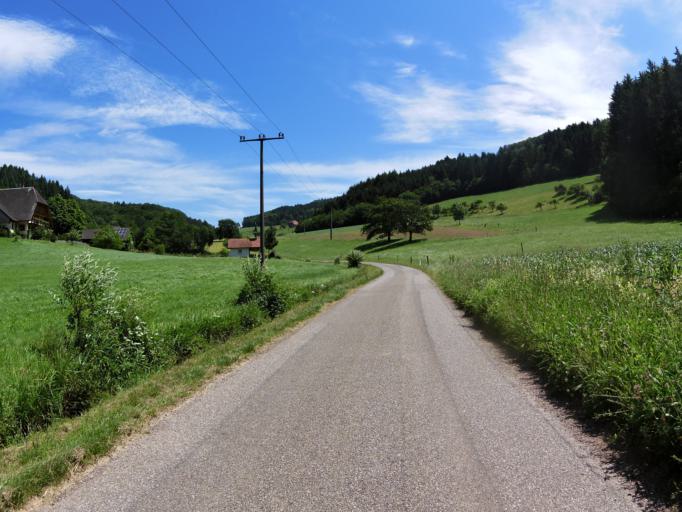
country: DE
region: Baden-Wuerttemberg
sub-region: Freiburg Region
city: Seelbach
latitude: 48.3229
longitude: 7.9622
